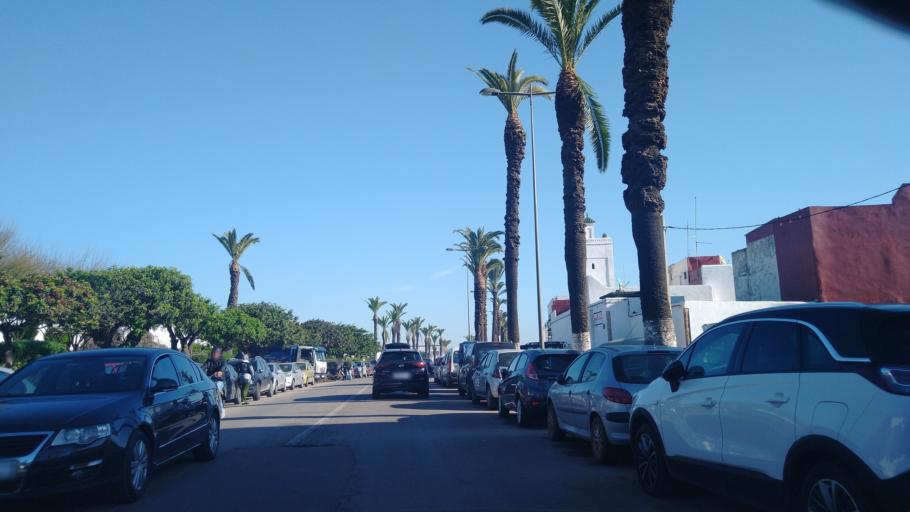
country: MA
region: Rabat-Sale-Zemmour-Zaer
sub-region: Rabat
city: Rabat
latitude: 34.0281
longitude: -6.8398
